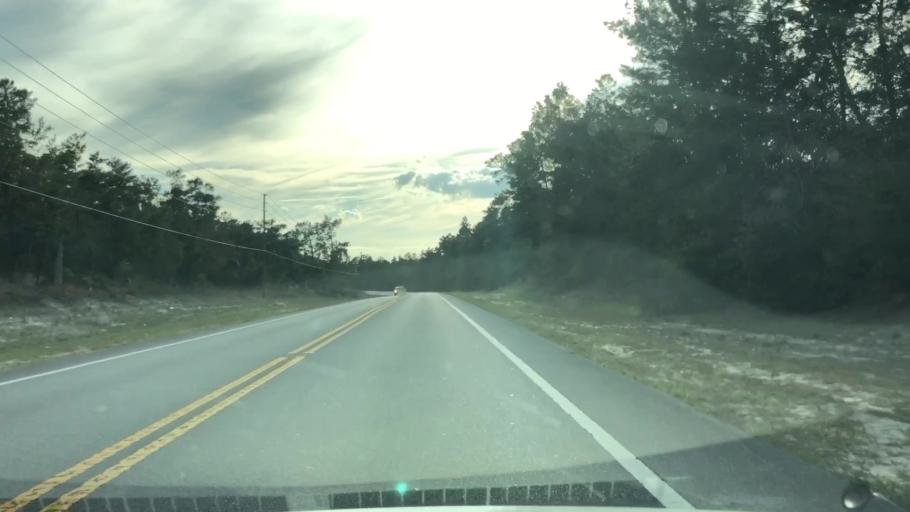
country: US
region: Florida
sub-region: Volusia County
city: Deltona
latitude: 28.9387
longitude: -81.2577
